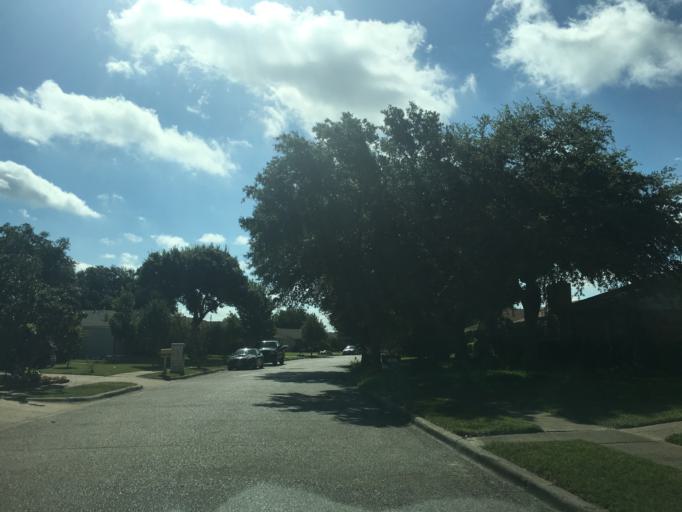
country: US
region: Texas
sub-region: Dallas County
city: Garland
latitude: 32.8515
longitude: -96.6565
